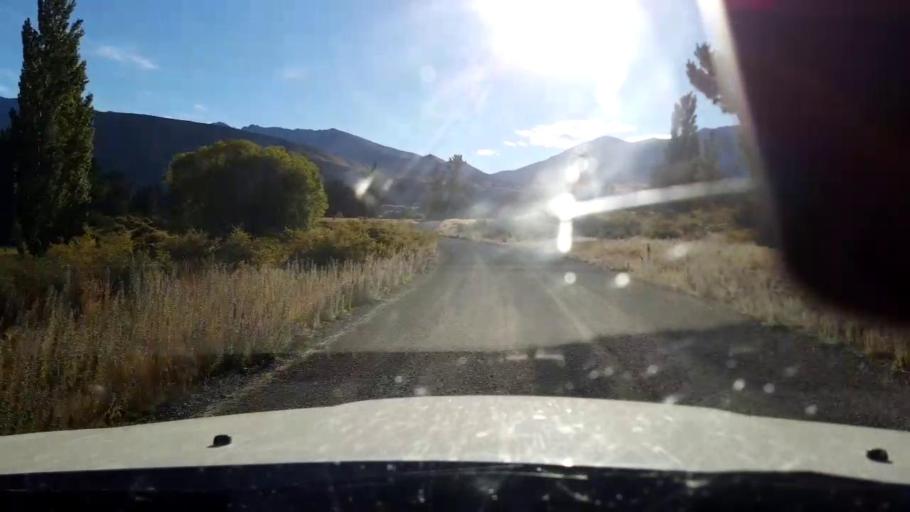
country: NZ
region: Canterbury
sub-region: Timaru District
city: Pleasant Point
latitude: -43.9642
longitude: 170.5245
